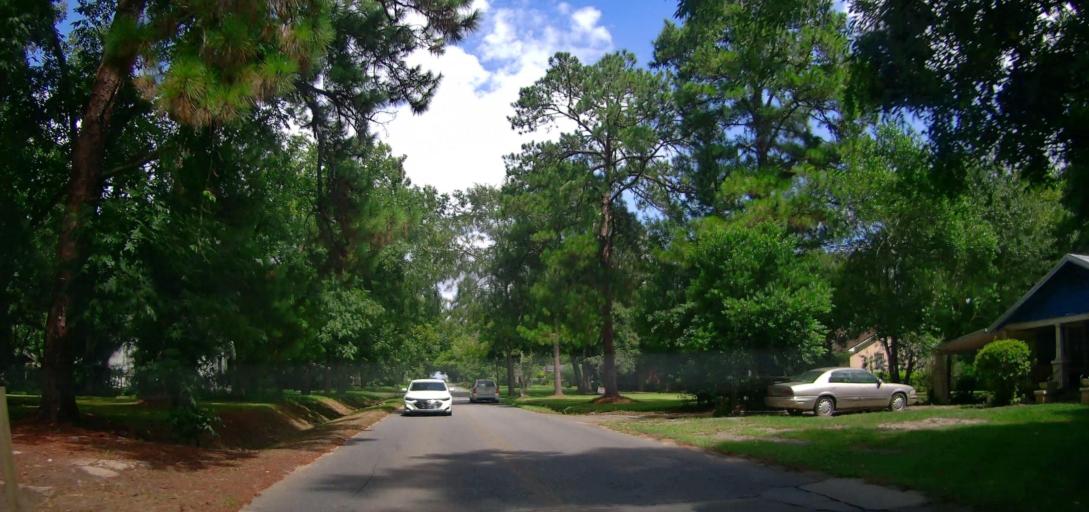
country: US
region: Georgia
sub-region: Ben Hill County
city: Fitzgerald
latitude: 31.7058
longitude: -83.2591
